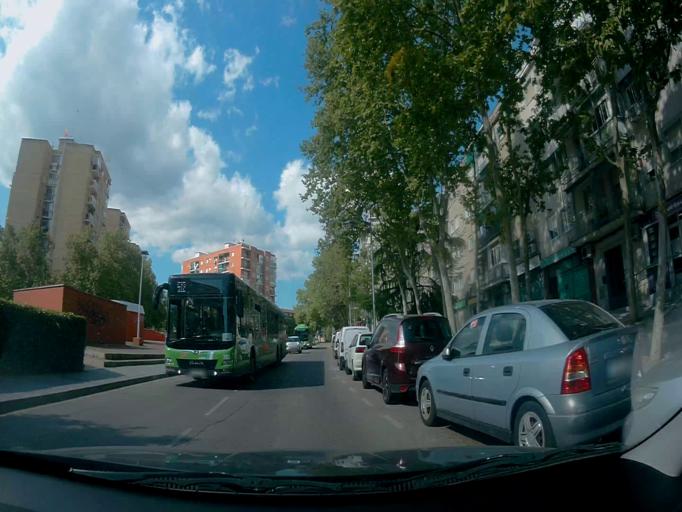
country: ES
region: Madrid
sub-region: Provincia de Madrid
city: Alcorcon
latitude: 40.3458
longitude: -3.8333
